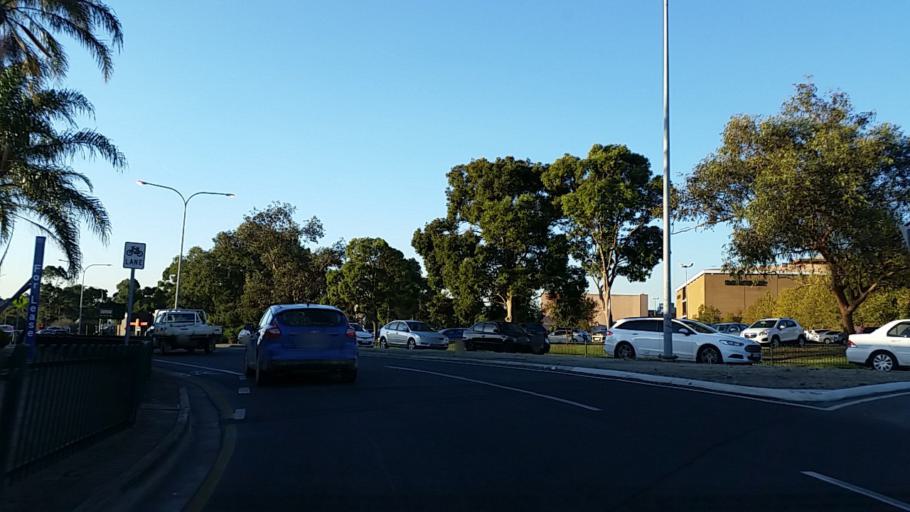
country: AU
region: South Australia
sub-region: Tea Tree Gully
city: Modbury
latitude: -34.8334
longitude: 138.6879
